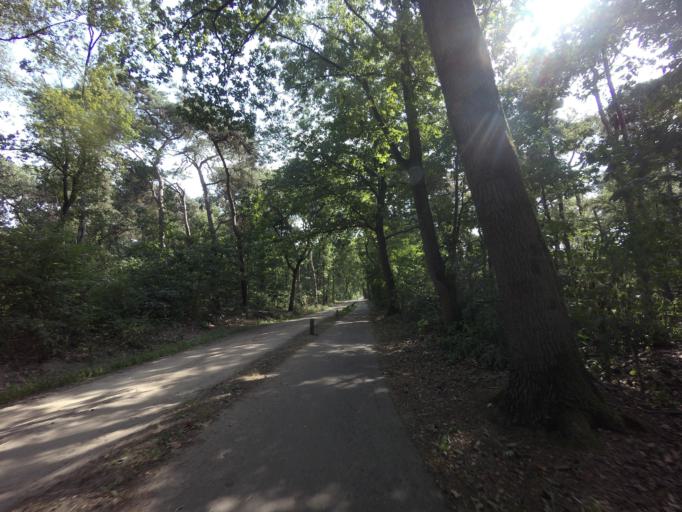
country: NL
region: North Brabant
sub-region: Gemeente Someren
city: Someren
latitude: 51.4034
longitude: 5.6762
